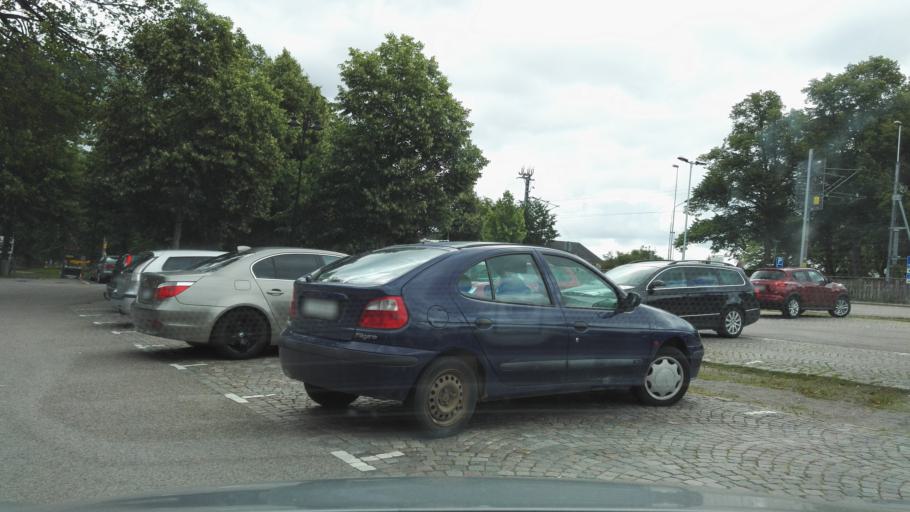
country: SE
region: Kronoberg
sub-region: Vaxjo Kommun
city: Vaexjoe
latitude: 56.8768
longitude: 14.8091
